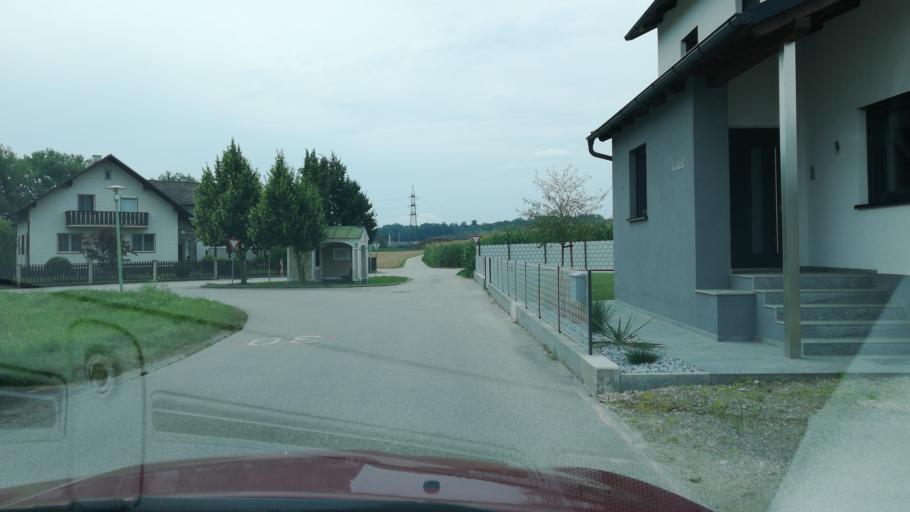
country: AT
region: Upper Austria
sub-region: Politischer Bezirk Urfahr-Umgebung
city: Feldkirchen an der Donau
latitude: 48.3047
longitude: 14.0119
